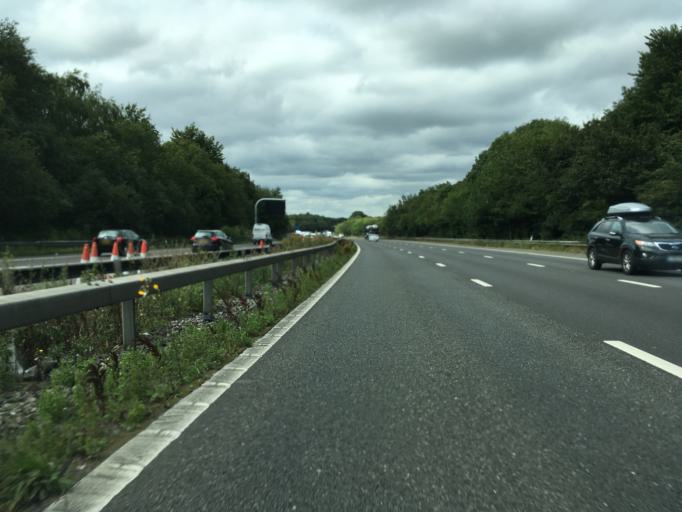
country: GB
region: England
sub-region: West Sussex
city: Maidenbower
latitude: 51.1189
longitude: -0.1381
